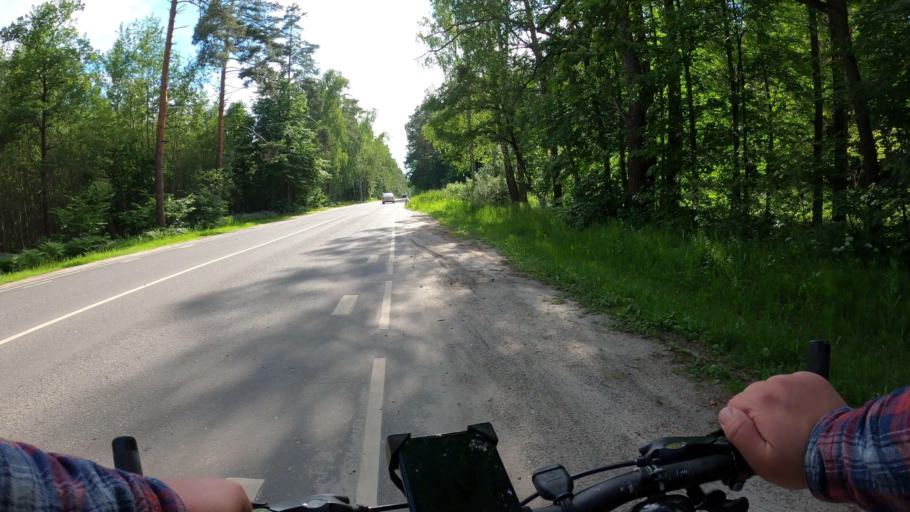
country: RU
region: Moskovskaya
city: Konobeyevo
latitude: 55.4354
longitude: 38.6579
